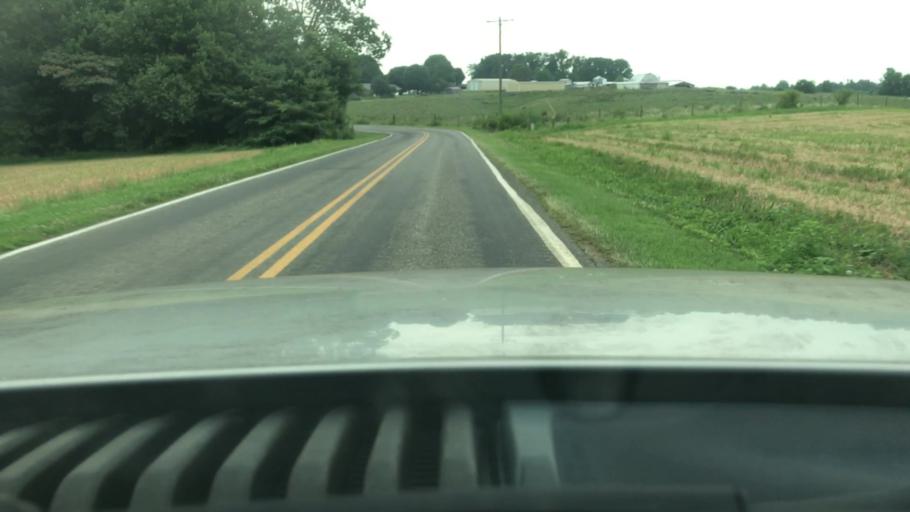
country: US
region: North Carolina
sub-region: Surry County
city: Dobson
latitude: 36.4047
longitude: -80.8086
